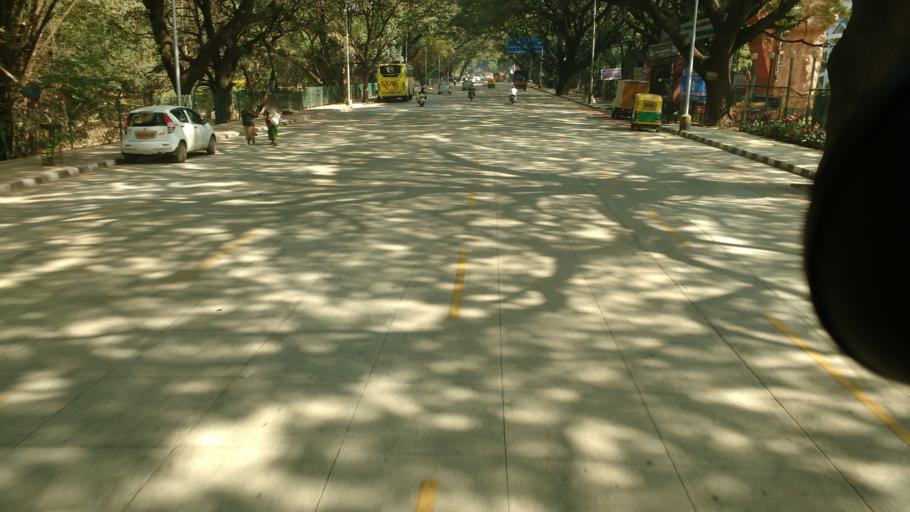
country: IN
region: Karnataka
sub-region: Bangalore Urban
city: Bangalore
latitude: 12.9702
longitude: 77.5917
